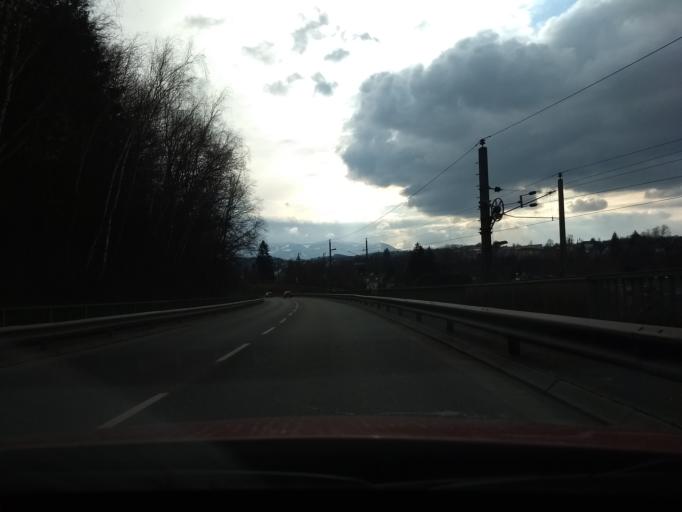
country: AT
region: Upper Austria
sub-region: Steyr Stadt
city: Steyr
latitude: 48.0349
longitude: 14.4198
